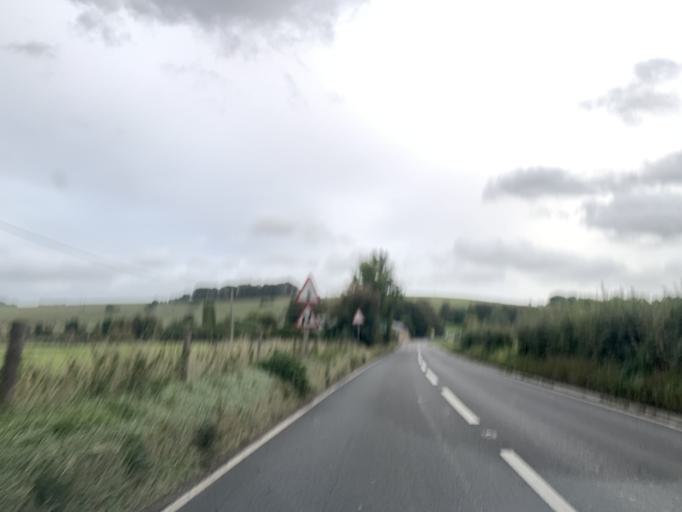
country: GB
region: England
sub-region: Wiltshire
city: Boyton
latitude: 51.1794
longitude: -2.0893
